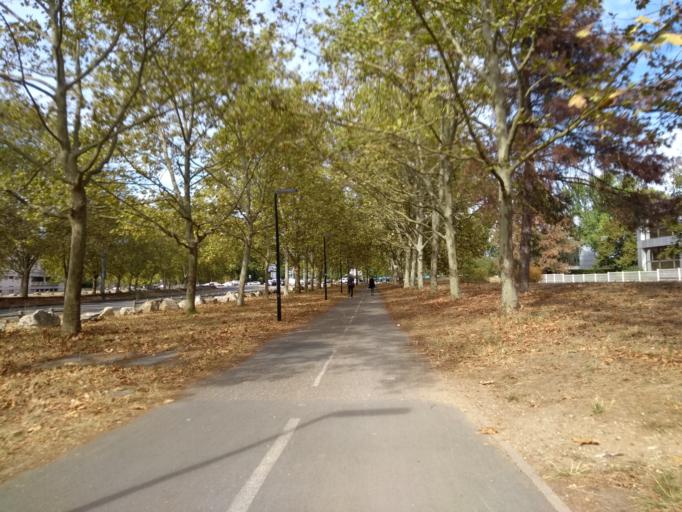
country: FR
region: Aquitaine
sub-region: Departement de la Gironde
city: Le Bouscat
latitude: 44.8757
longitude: -0.5766
